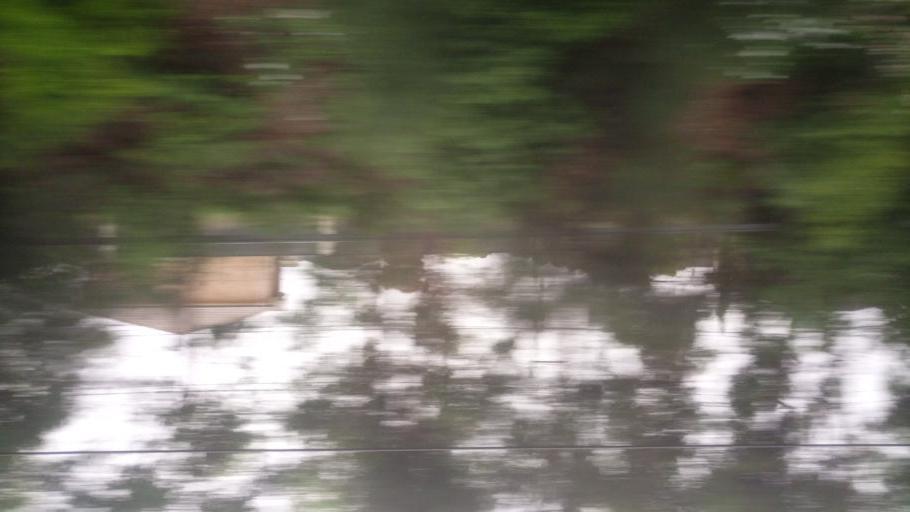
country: AU
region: New South Wales
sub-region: Blacktown
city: Doonside
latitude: -33.7633
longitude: 150.8749
